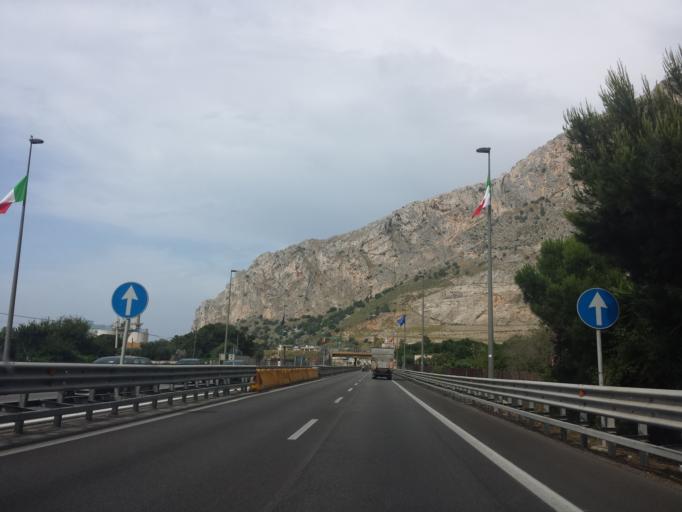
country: IT
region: Sicily
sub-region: Palermo
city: Isola delle Femmine
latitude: 38.1842
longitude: 13.2472
